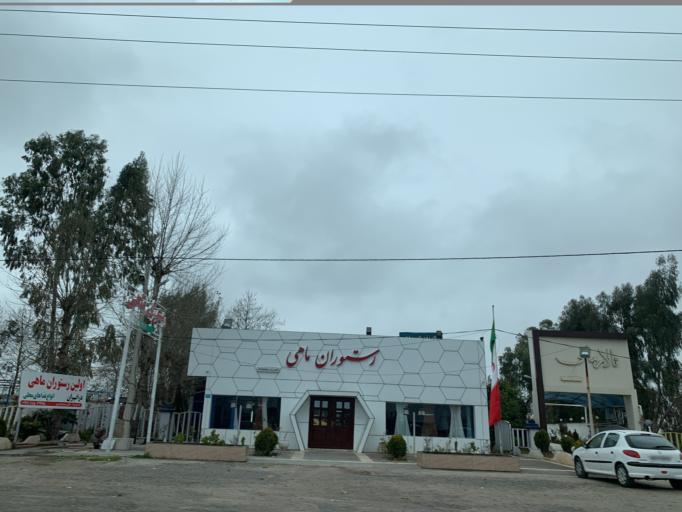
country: IR
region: Mazandaran
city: Babol
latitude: 36.5237
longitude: 52.6081
